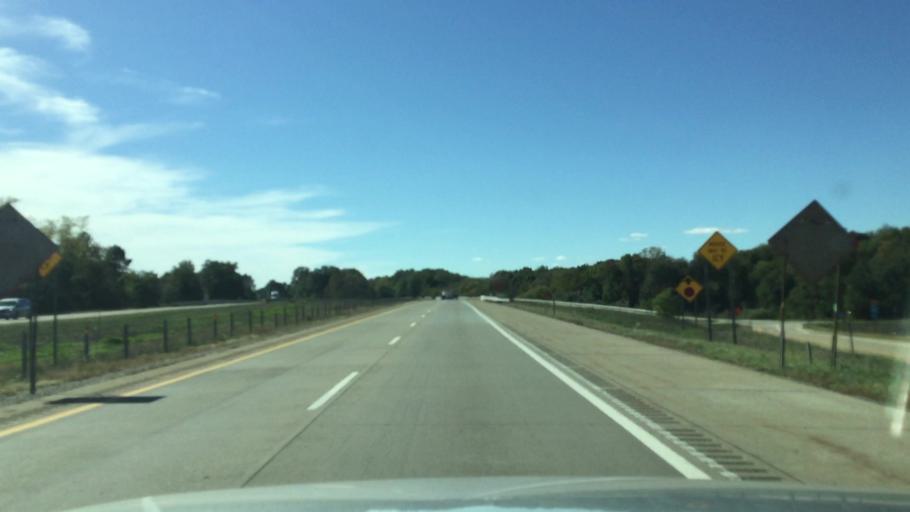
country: US
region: Michigan
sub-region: Jackson County
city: Grass Lake
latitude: 42.2919
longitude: -84.2575
